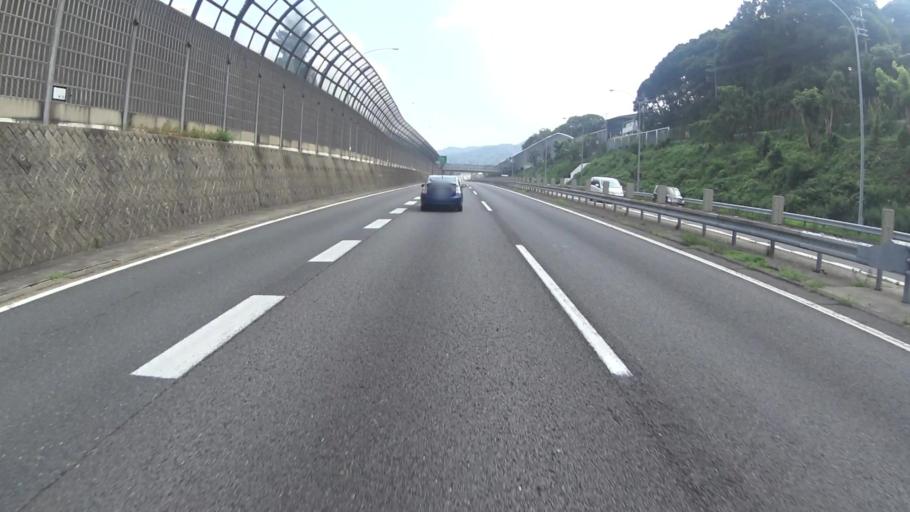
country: JP
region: Shiga Prefecture
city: Otsu-shi
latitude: 34.9770
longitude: 135.8288
